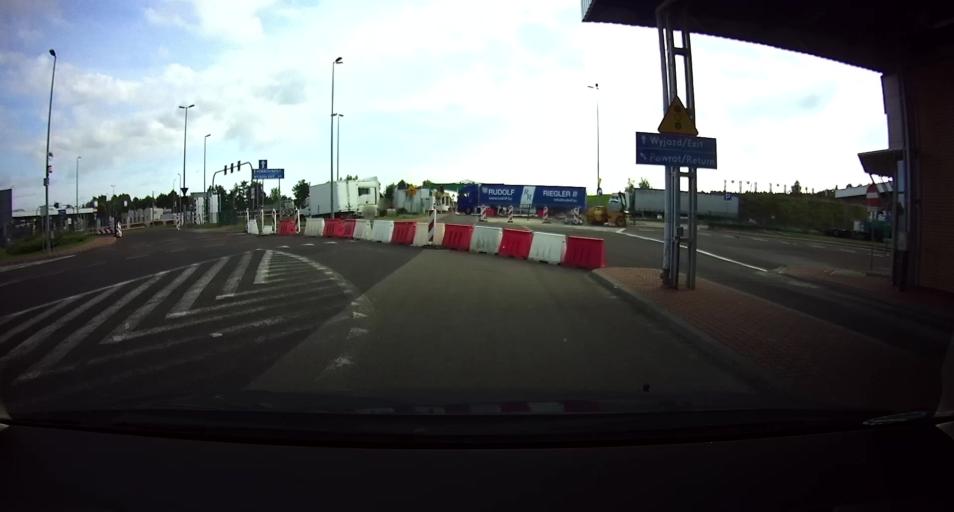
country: PL
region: Podlasie
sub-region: Powiat sokolski
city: Kuznica
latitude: 53.5210
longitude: 23.6584
